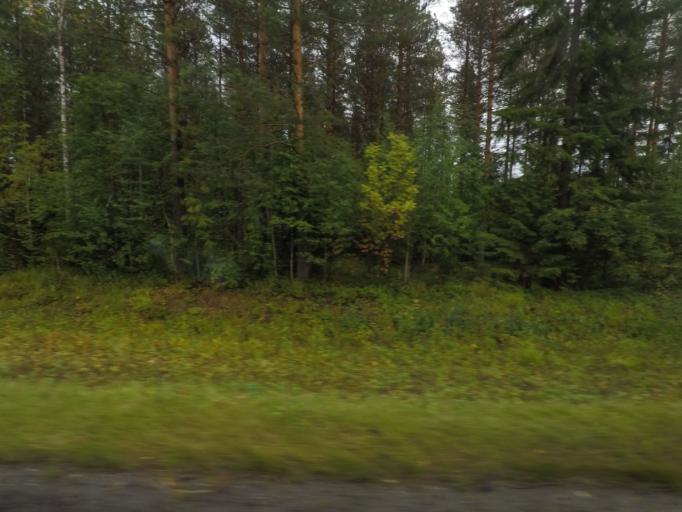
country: FI
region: Southern Savonia
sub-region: Pieksaemaeki
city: Joroinen
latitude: 62.1297
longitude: 27.8391
